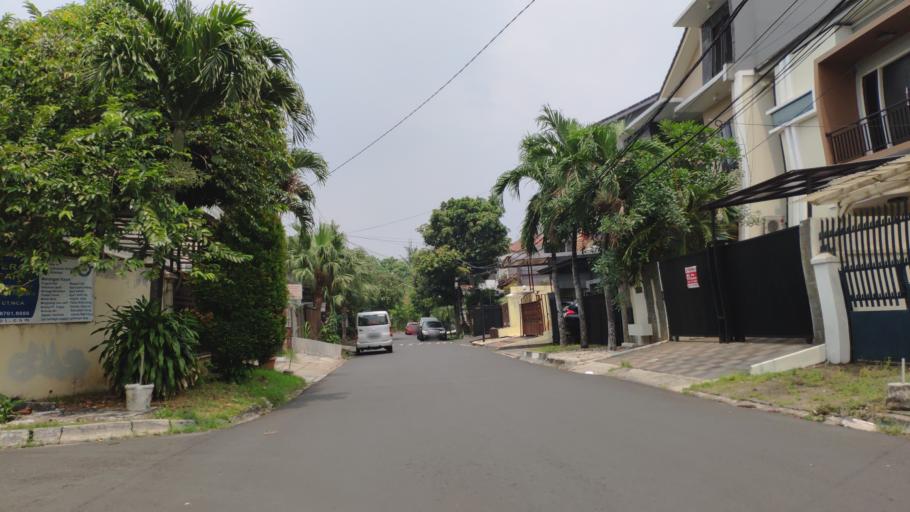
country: ID
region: Banten
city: South Tangerang
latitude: -6.2697
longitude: 106.7778
